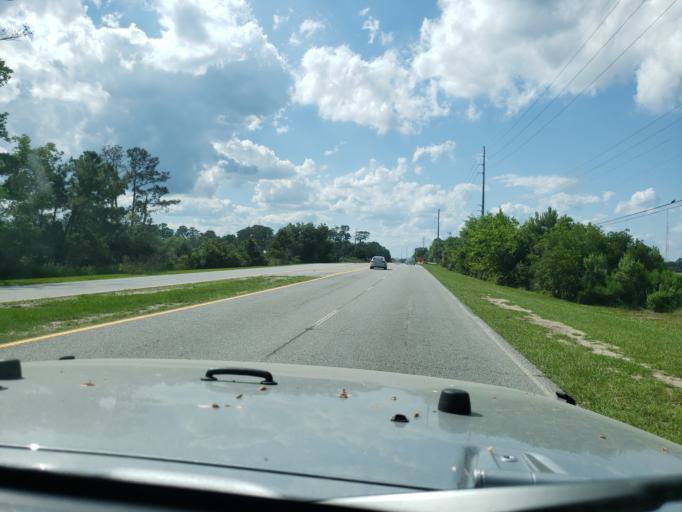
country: US
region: Georgia
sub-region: Chatham County
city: Whitemarsh Island
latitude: 32.0497
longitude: -81.0107
